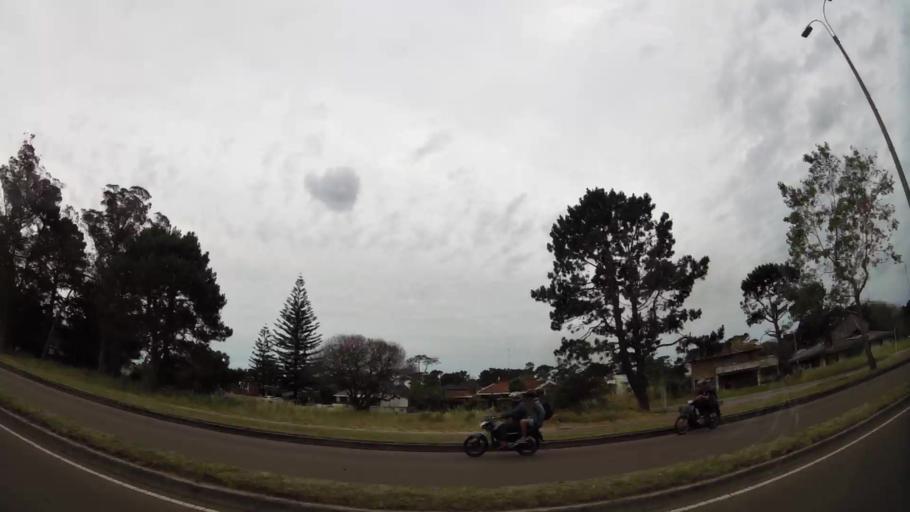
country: UY
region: Maldonado
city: Maldonado
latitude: -34.9208
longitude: -54.9543
